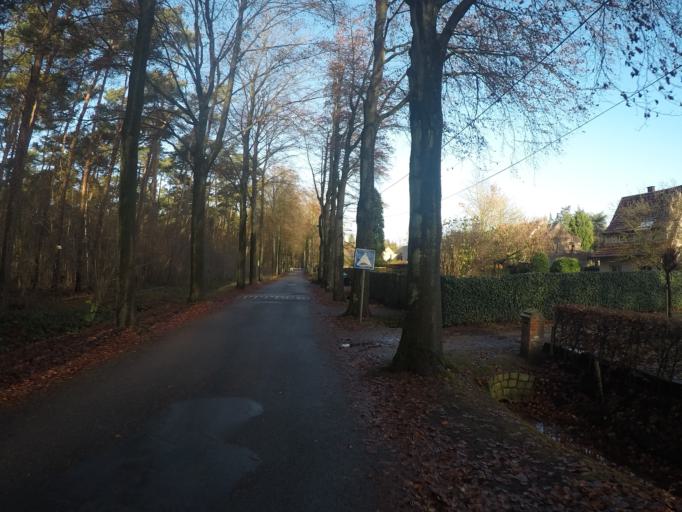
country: BE
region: Flanders
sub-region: Provincie Antwerpen
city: Brasschaat
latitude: 51.2892
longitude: 4.5354
